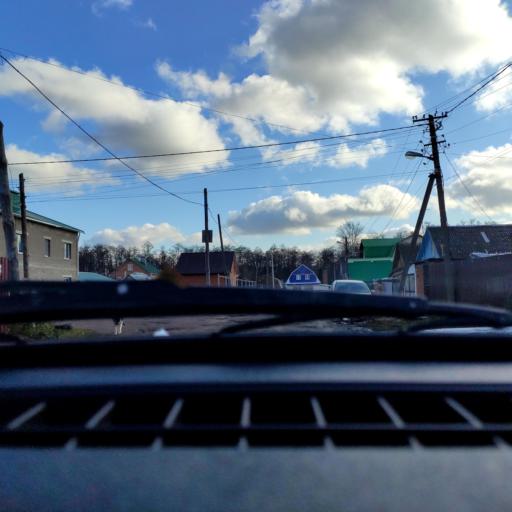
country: RU
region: Bashkortostan
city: Ufa
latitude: 54.8170
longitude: 56.1654
